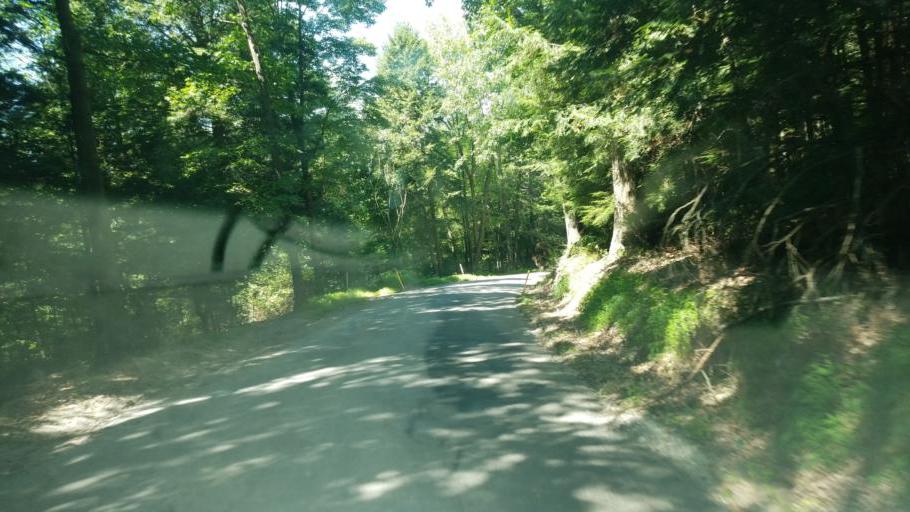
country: US
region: Pennsylvania
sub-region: Clarion County
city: Knox
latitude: 41.1870
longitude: -79.5125
